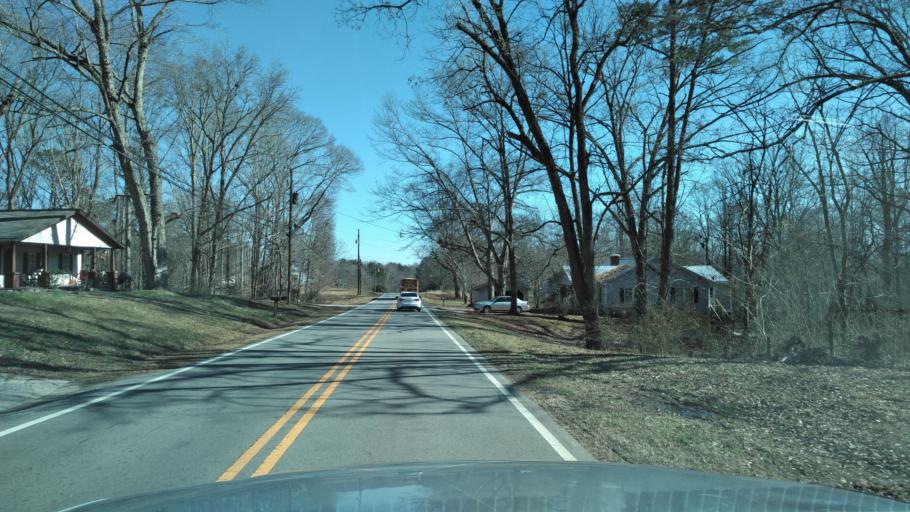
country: US
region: Georgia
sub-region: Hall County
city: Gainesville
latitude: 34.3155
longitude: -83.7501
